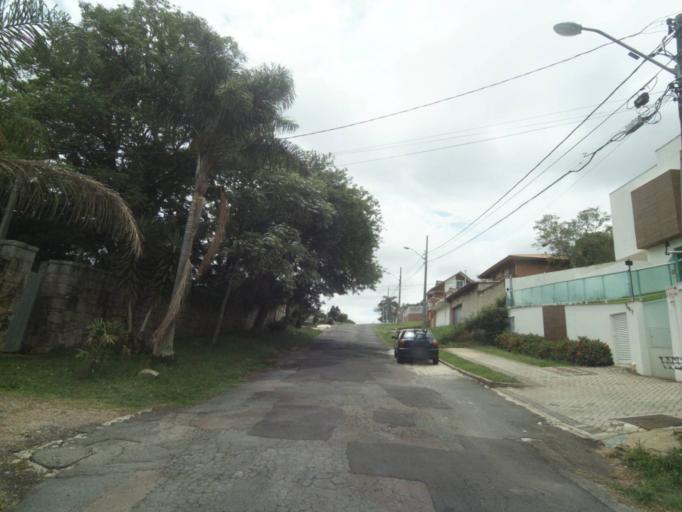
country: BR
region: Parana
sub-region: Curitiba
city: Curitiba
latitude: -25.3923
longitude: -49.2892
